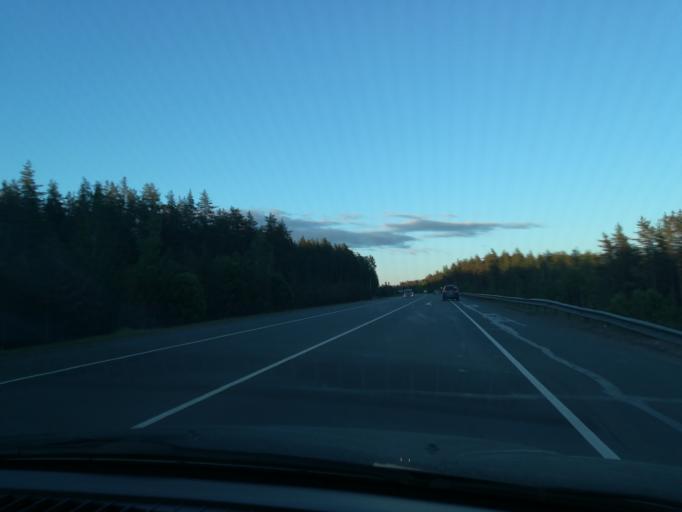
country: RU
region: Leningrad
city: Yakovlevo
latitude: 60.3614
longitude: 29.5696
